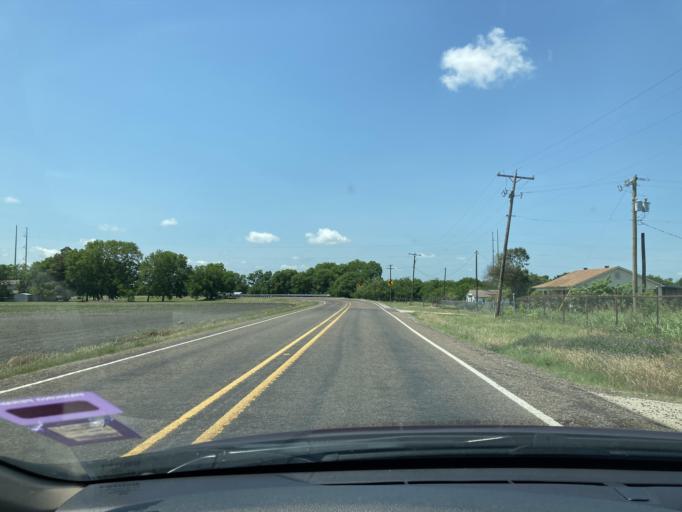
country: US
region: Texas
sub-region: Navarro County
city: Kerens
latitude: 32.1094
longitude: -96.3219
